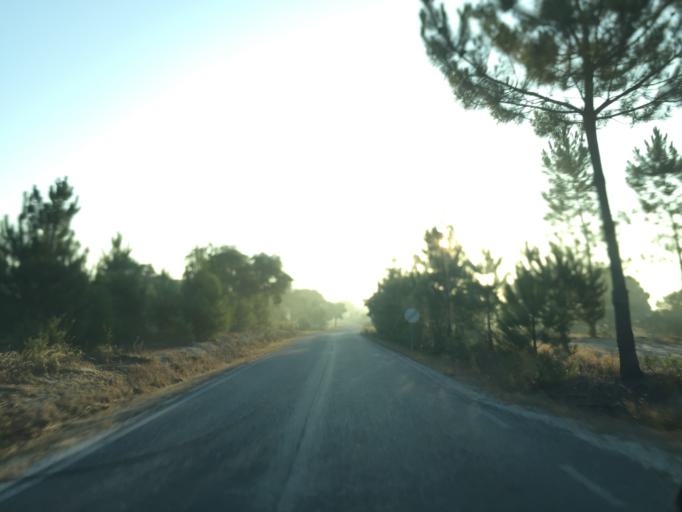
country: PT
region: Santarem
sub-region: Coruche
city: Coruche
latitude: 39.0430
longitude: -8.4369
